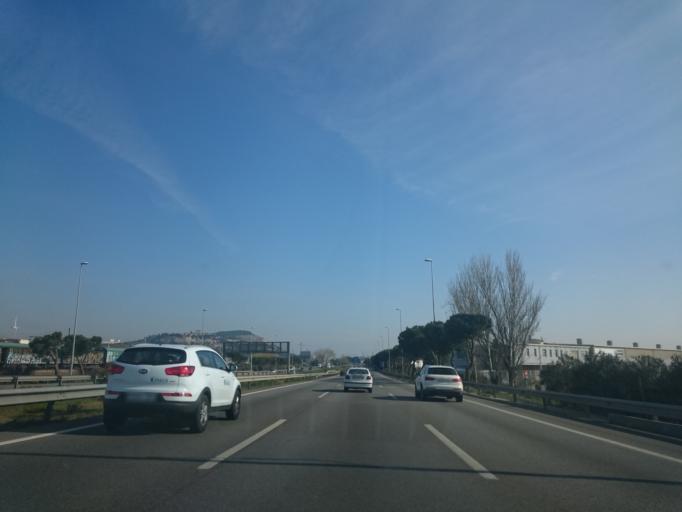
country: ES
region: Catalonia
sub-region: Provincia de Barcelona
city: Sants-Montjuic
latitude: 41.3448
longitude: 2.1356
